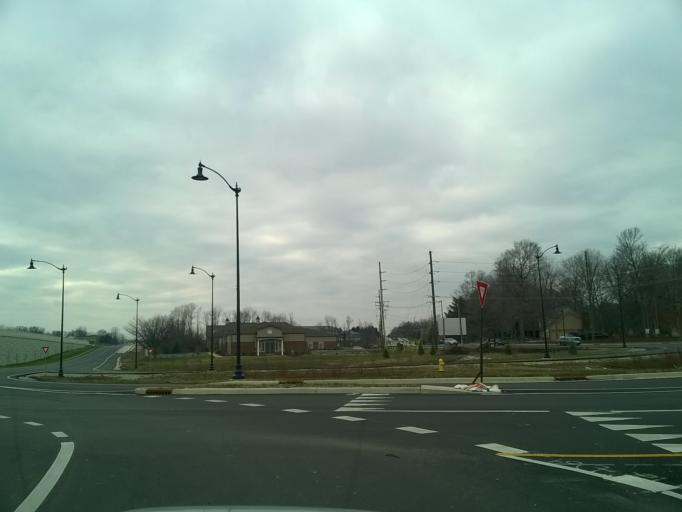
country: US
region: Indiana
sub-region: Hamilton County
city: Carmel
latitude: 39.9846
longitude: -86.1435
